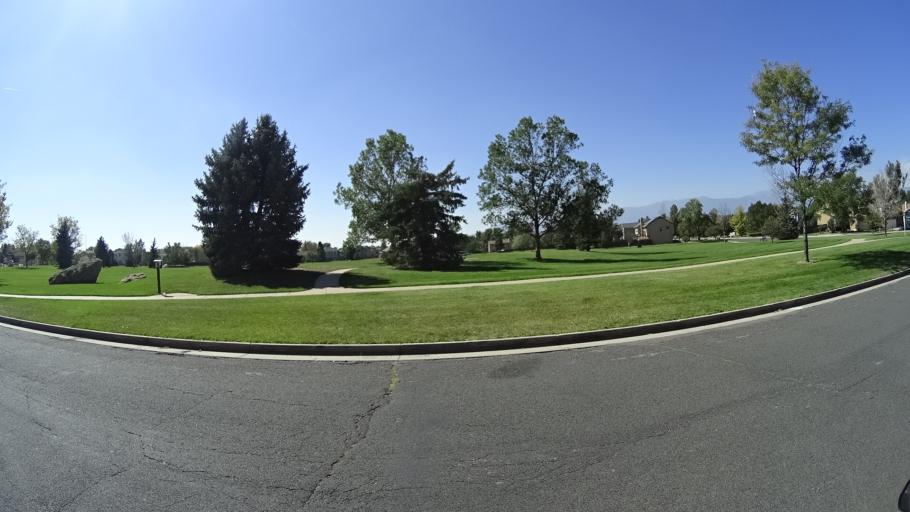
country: US
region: Colorado
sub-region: El Paso County
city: Cimarron Hills
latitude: 38.8998
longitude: -104.6996
